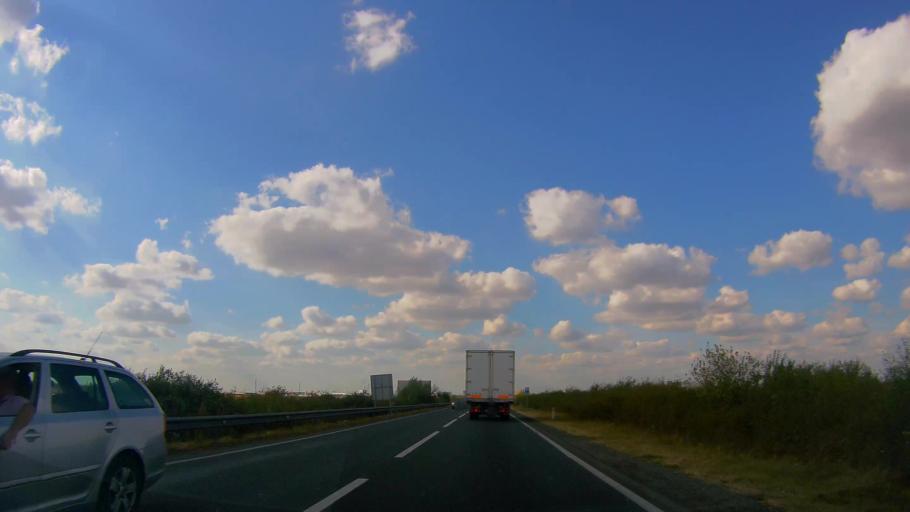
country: RO
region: Satu Mare
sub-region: Oras Ardud
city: Madaras
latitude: 47.7241
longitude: 22.8877
